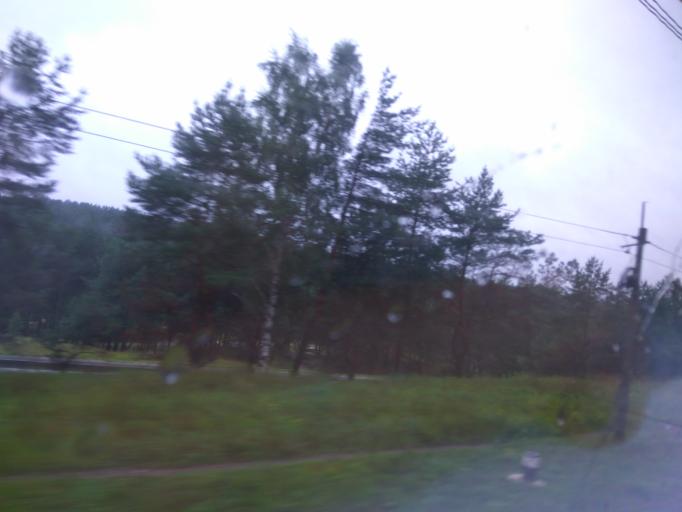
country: RU
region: Moskovskaya
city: Stupino
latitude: 54.8746
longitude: 38.1178
